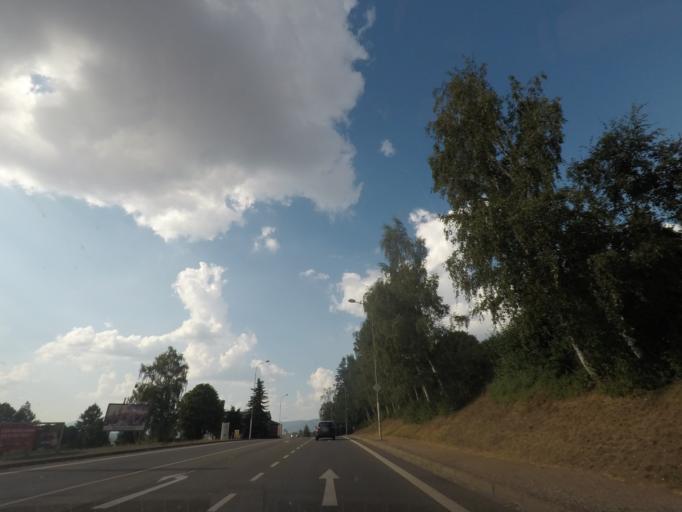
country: CZ
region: Kralovehradecky
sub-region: Okres Trutnov
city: Trutnov
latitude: 50.5544
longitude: 15.9043
